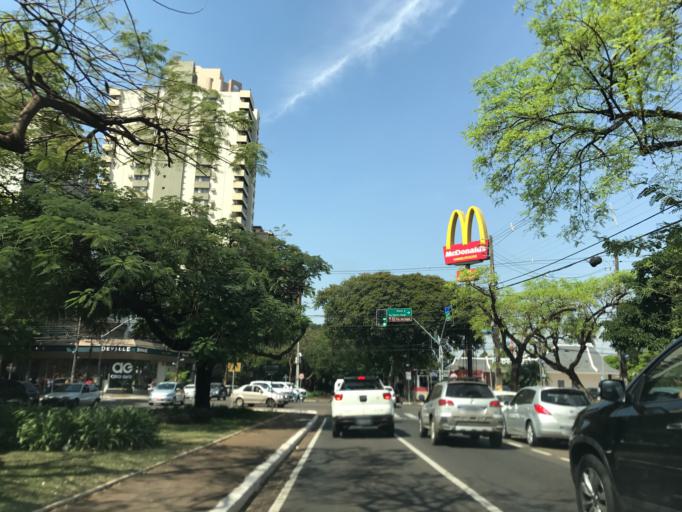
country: BR
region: Parana
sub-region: Maringa
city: Maringa
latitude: -23.4257
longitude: -51.9372
